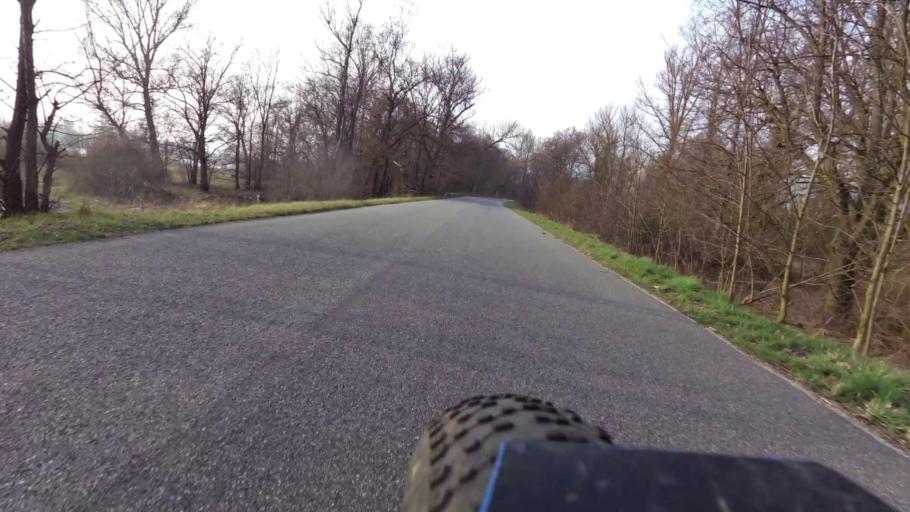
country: DE
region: Brandenburg
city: Vogelsang
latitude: 52.2495
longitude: 14.7049
